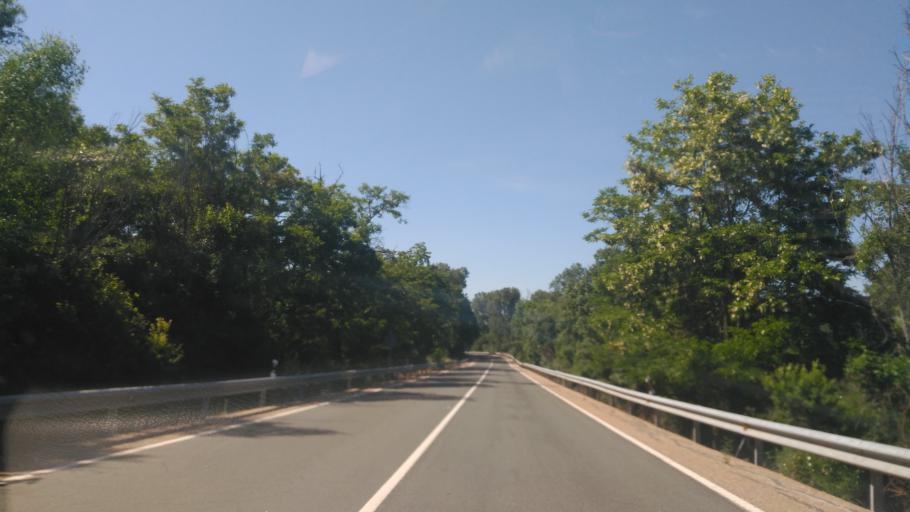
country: ES
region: Castille and Leon
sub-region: Provincia de Zamora
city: Corrales
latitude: 41.3089
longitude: -5.7281
